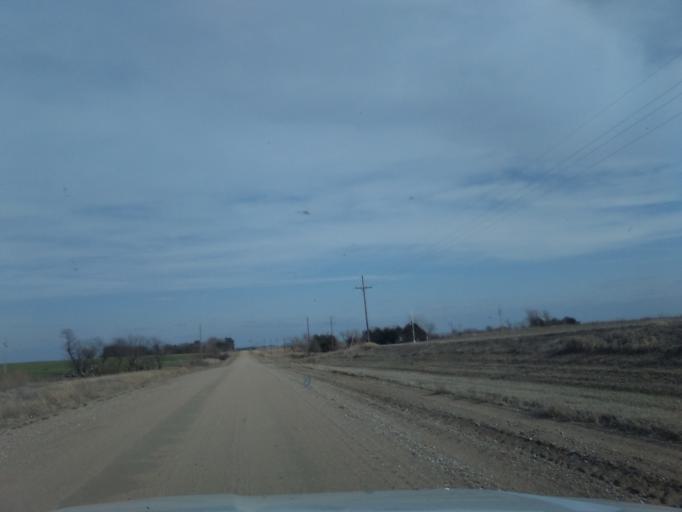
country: US
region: Nebraska
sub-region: Jefferson County
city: Fairbury
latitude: 40.2191
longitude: -97.1927
